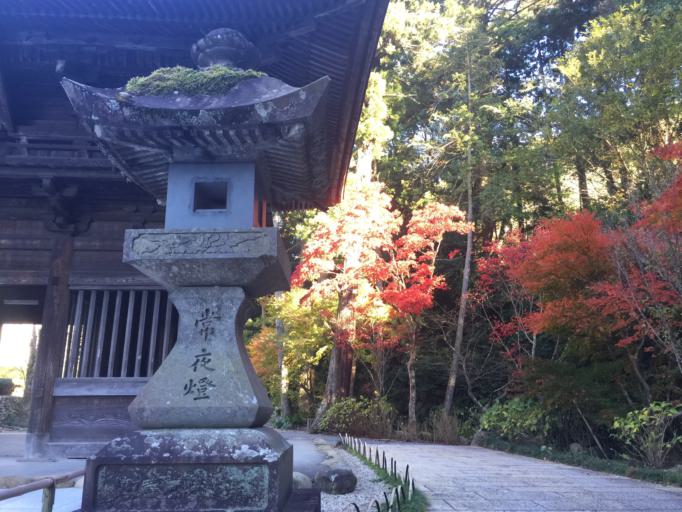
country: JP
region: Shizuoka
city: Kakegawa
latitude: 34.7345
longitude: 137.9728
